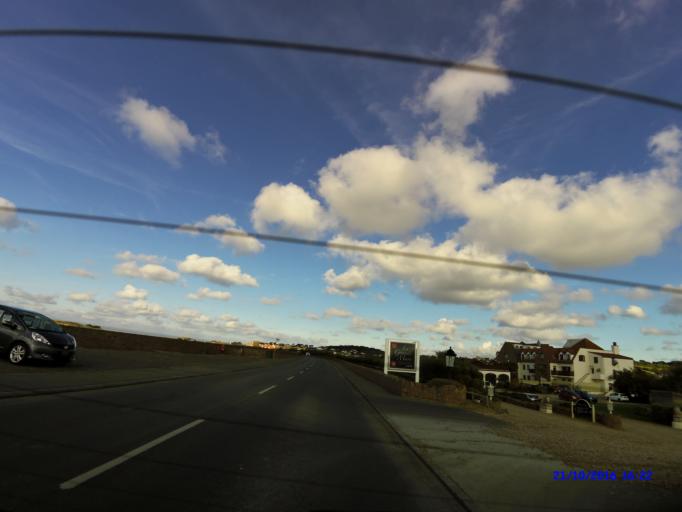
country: GG
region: St Peter Port
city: Saint Peter Port
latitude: 49.4660
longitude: -2.6091
